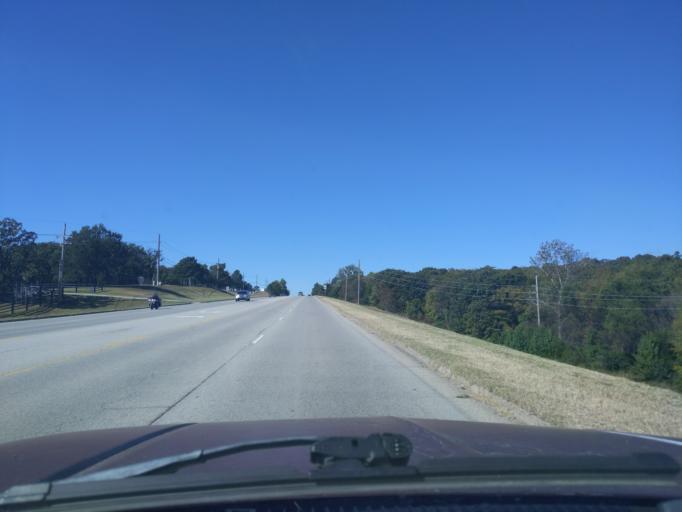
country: US
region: Oklahoma
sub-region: Tulsa County
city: Glenpool
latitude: 35.9885
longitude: -96.0395
